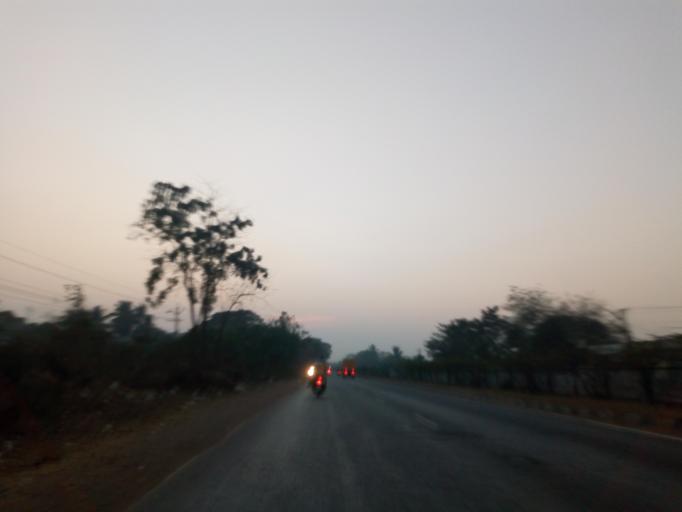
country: IN
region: Andhra Pradesh
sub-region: West Godavari
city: Tadepallegudem
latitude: 16.8234
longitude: 81.4207
